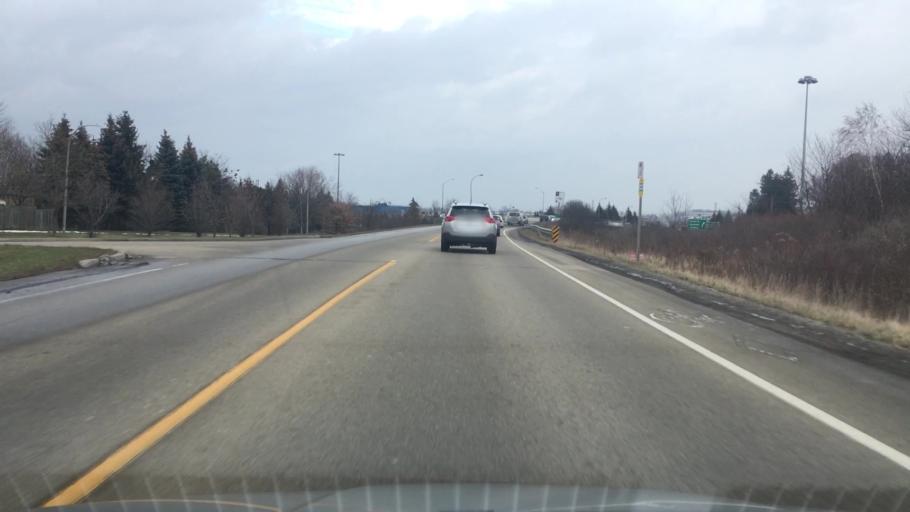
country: CA
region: Ontario
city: Ancaster
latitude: 43.2248
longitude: -79.9596
